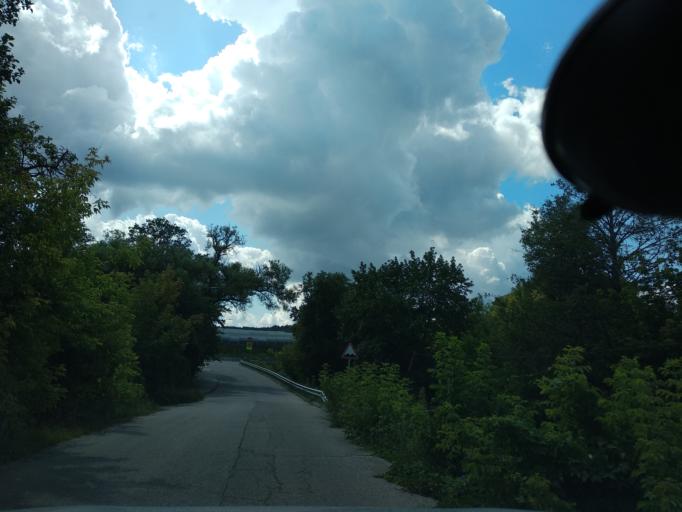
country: LT
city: Grigiskes
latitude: 54.6795
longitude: 25.0775
